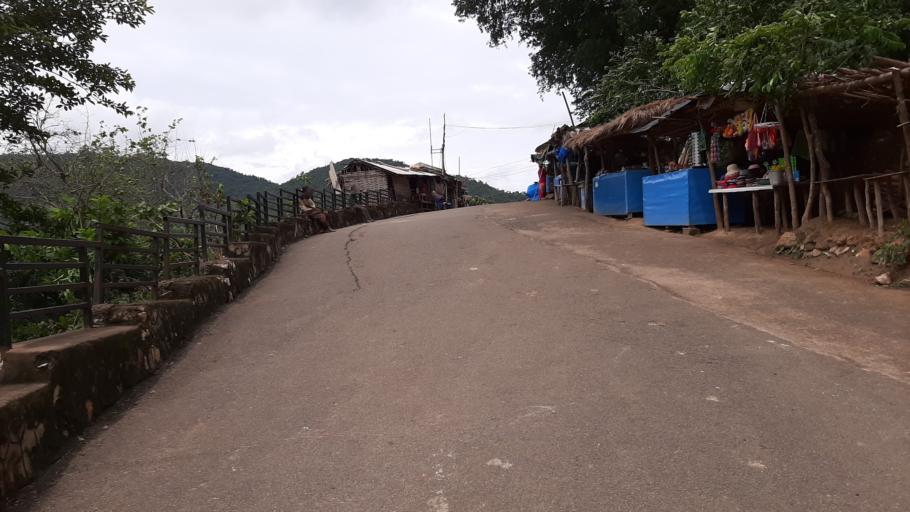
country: IN
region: Andhra Pradesh
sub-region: Vizianagaram District
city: Salur
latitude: 18.2796
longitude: 83.0381
